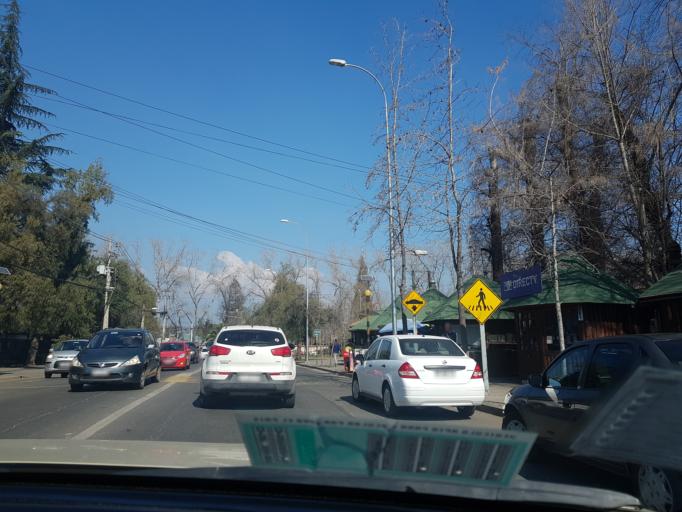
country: CL
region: Santiago Metropolitan
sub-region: Provincia de Cordillera
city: Puente Alto
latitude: -33.6345
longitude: -70.5735
